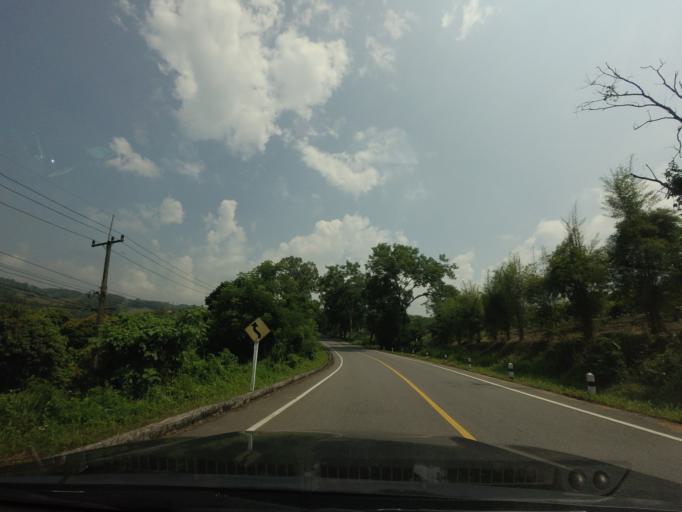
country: TH
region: Nan
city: Santi Suk
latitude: 18.9000
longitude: 100.8427
